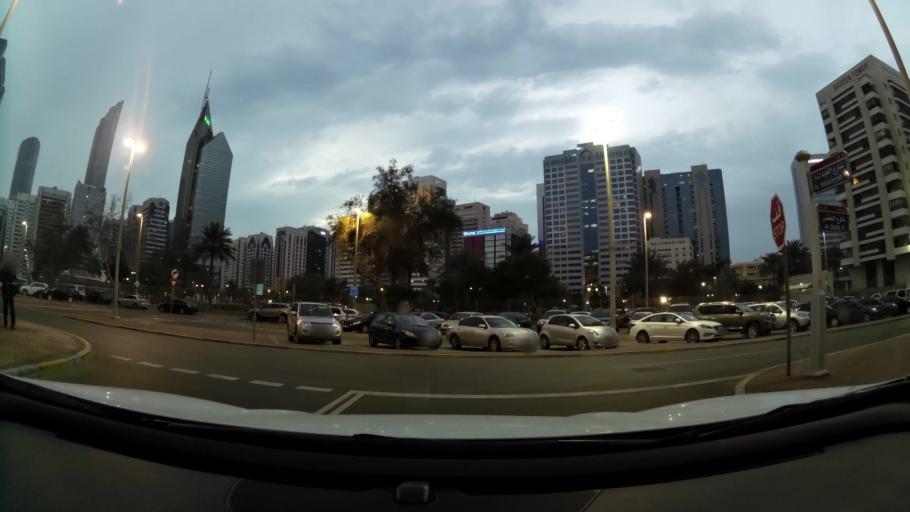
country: AE
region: Abu Dhabi
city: Abu Dhabi
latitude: 24.4919
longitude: 54.3657
